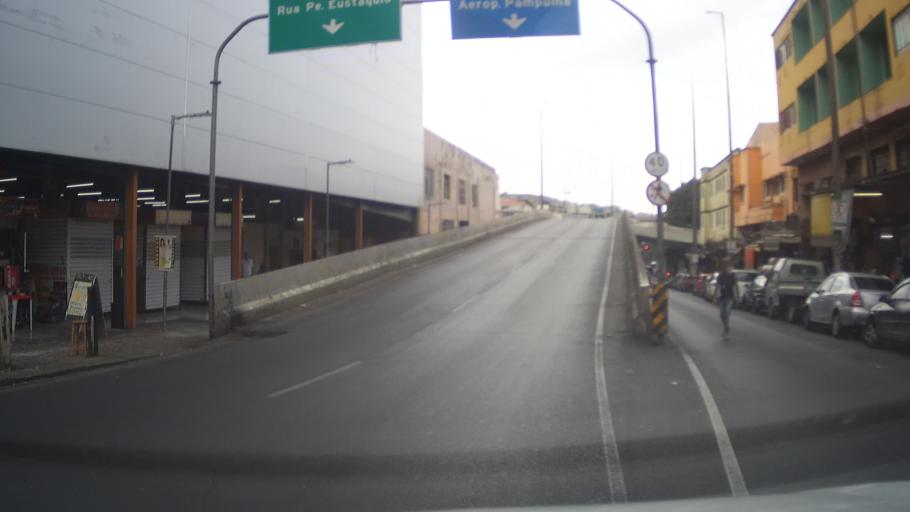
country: BR
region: Minas Gerais
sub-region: Belo Horizonte
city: Belo Horizonte
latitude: -19.9145
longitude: -43.9403
